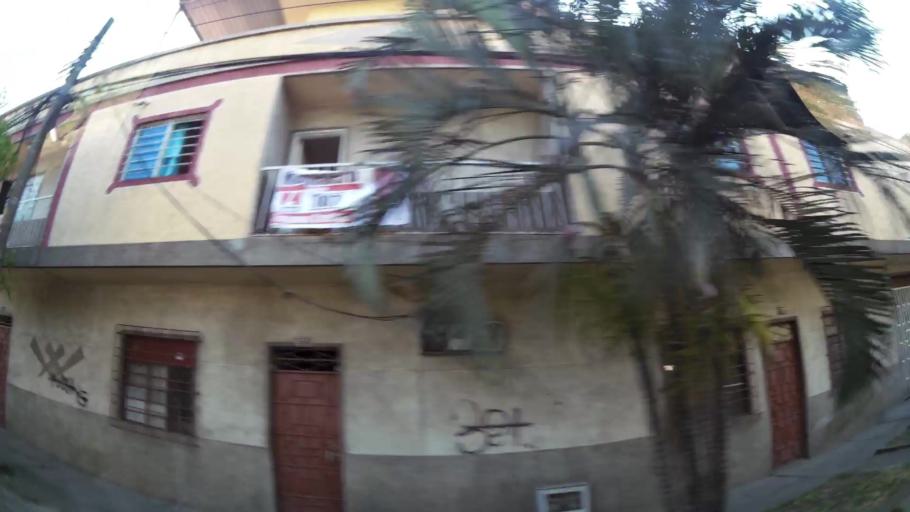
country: CO
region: Valle del Cauca
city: Cali
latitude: 3.4234
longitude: -76.5206
